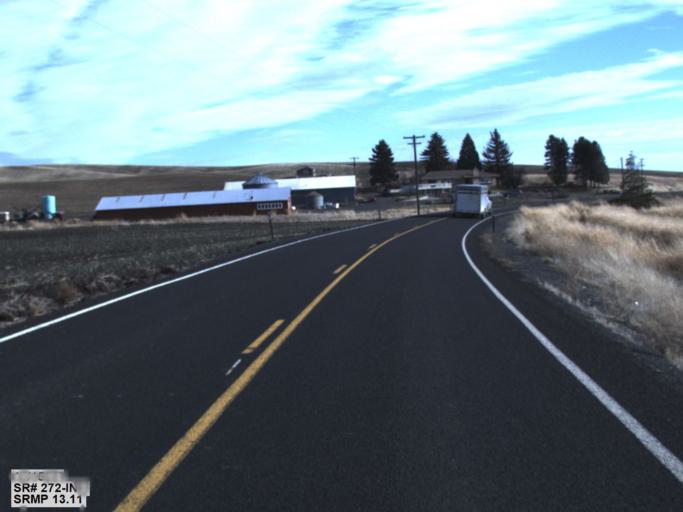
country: US
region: Washington
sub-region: Whitman County
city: Pullman
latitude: 46.9323
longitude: -117.1273
